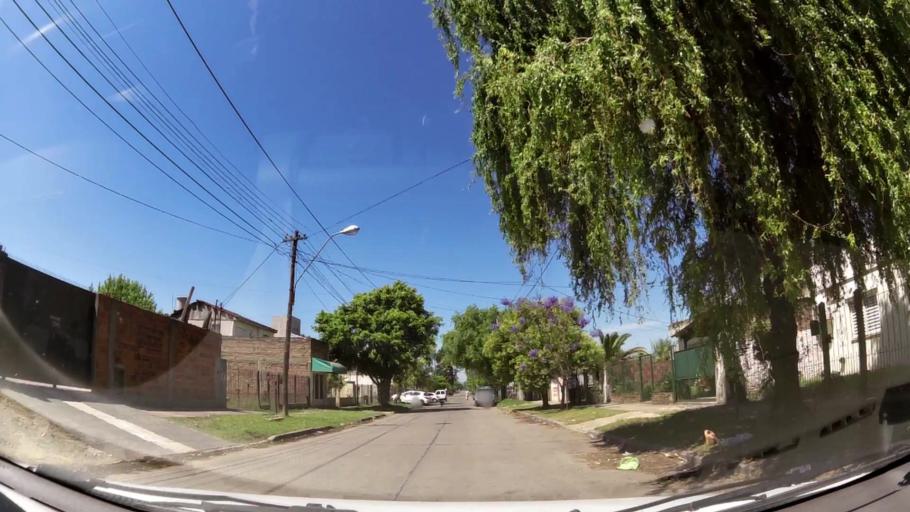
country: AR
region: Buenos Aires
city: Ituzaingo
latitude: -34.6844
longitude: -58.6578
